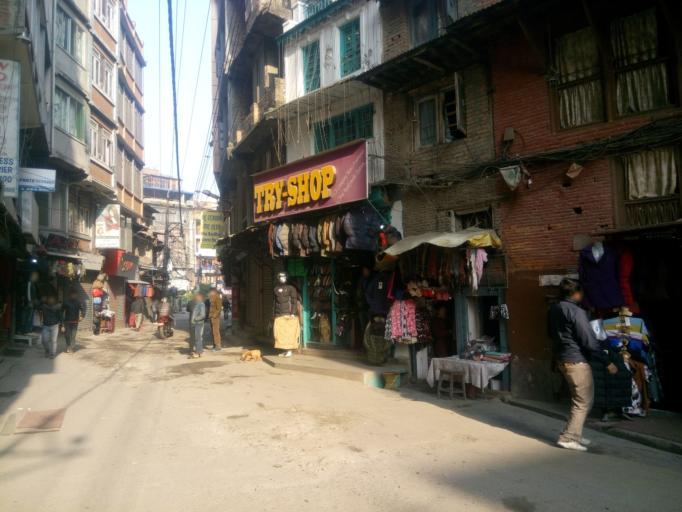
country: NP
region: Central Region
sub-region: Bagmati Zone
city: Kathmandu
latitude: 27.7008
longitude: 85.3115
